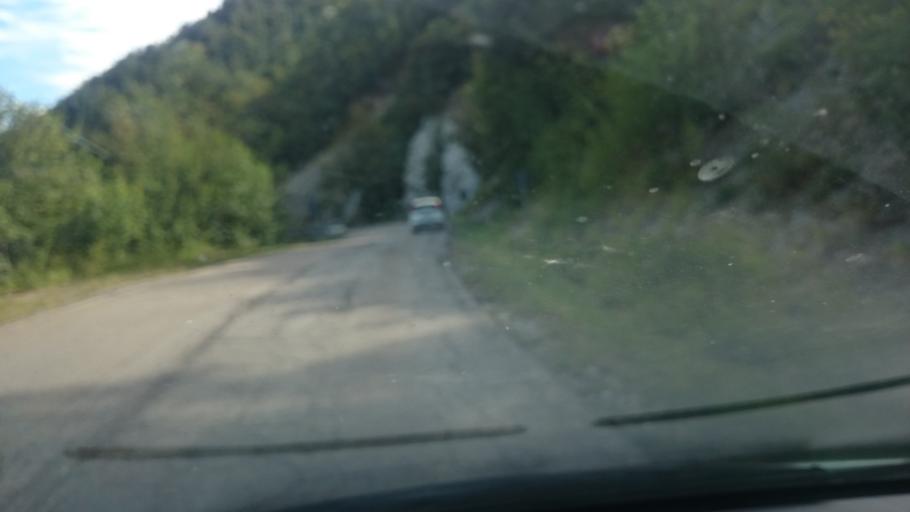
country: IT
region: Emilia-Romagna
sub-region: Provincia di Reggio Emilia
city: Villa Minozzo
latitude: 44.3258
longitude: 10.4601
